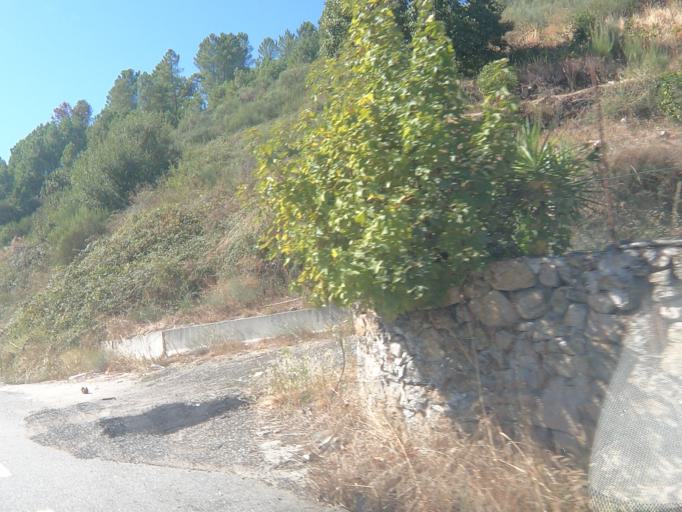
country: PT
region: Vila Real
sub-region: Vila Real
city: Vila Real
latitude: 41.2767
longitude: -7.7654
